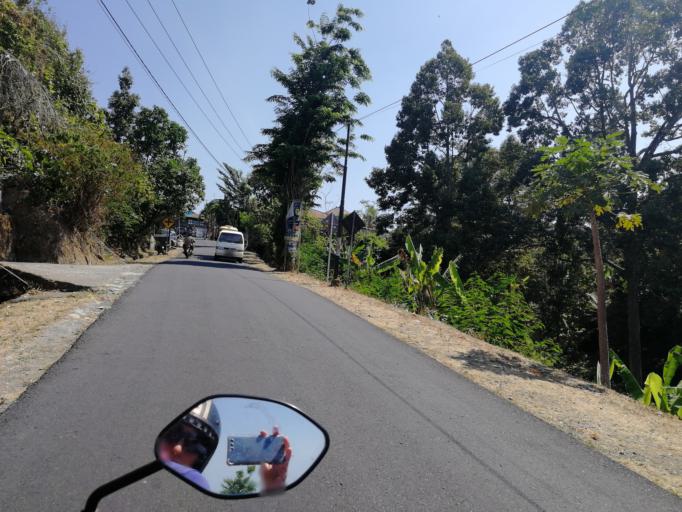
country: ID
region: Bali
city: Banjar Kedisan
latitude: -8.1481
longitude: 115.3065
